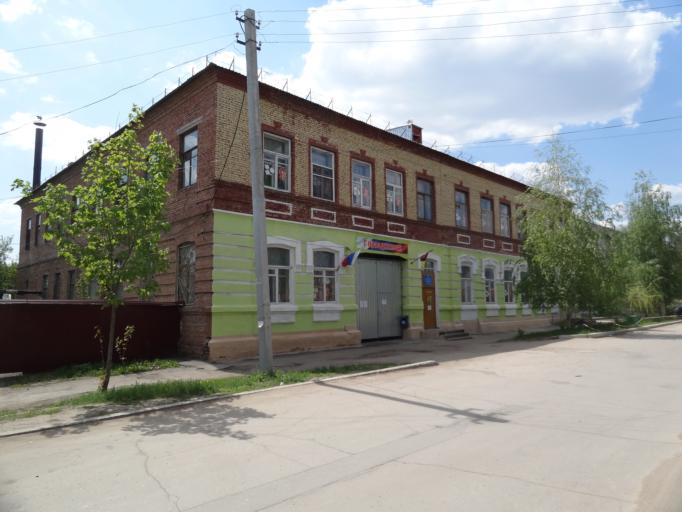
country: RU
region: Saratov
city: Engel's
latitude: 51.4992
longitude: 46.1352
